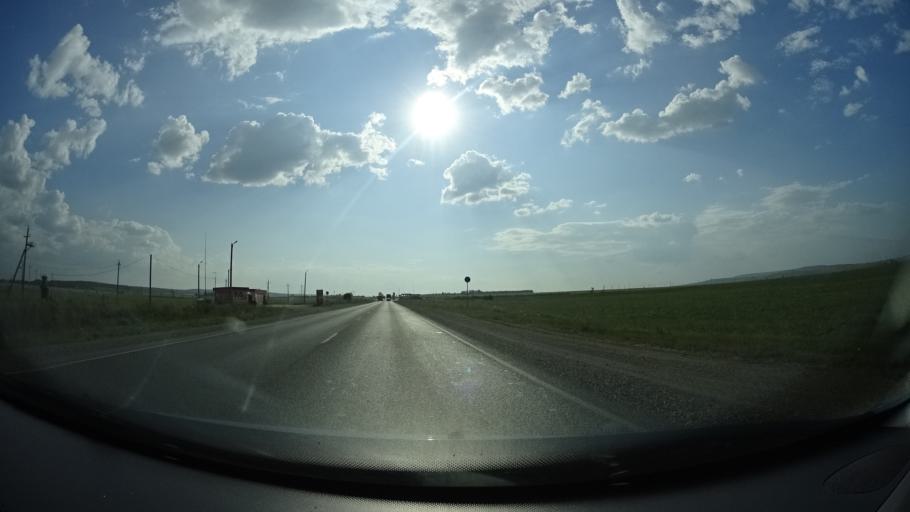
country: RU
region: Bashkortostan
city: Oktyabr'skiy
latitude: 54.4820
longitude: 53.3799
